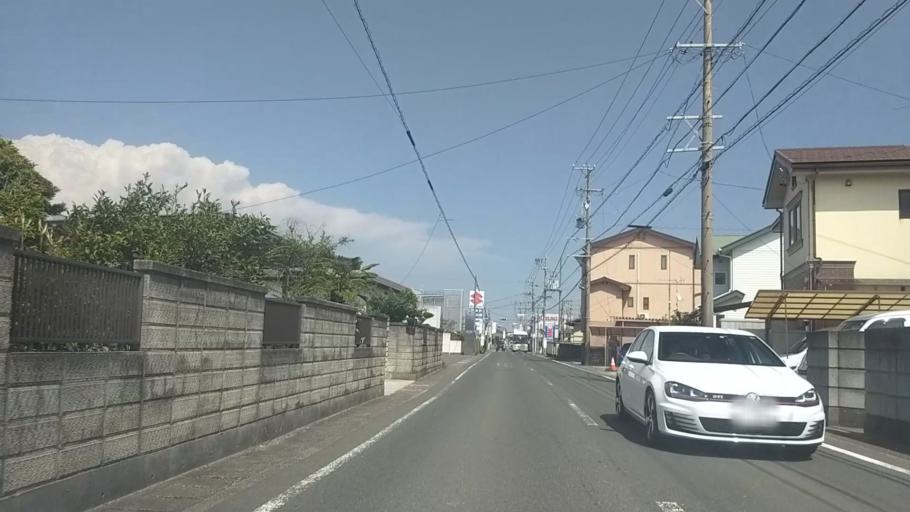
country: JP
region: Shizuoka
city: Hamamatsu
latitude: 34.6813
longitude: 137.6964
